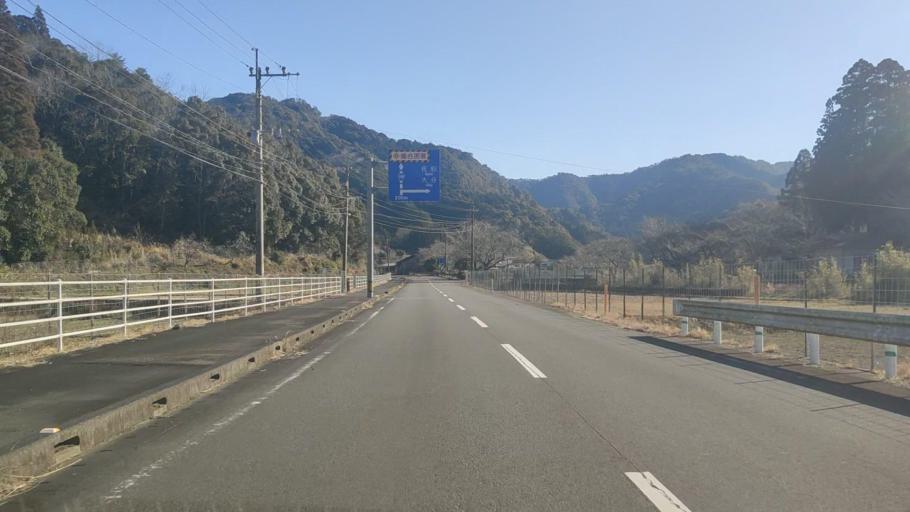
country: JP
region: Oita
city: Saiki
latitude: 32.7741
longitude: 131.8260
